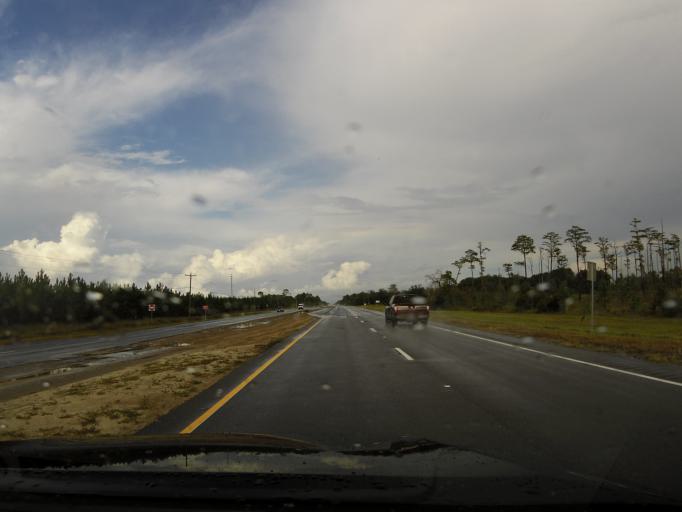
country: US
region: Georgia
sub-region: Long County
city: Ludowici
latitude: 31.7260
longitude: -81.7217
